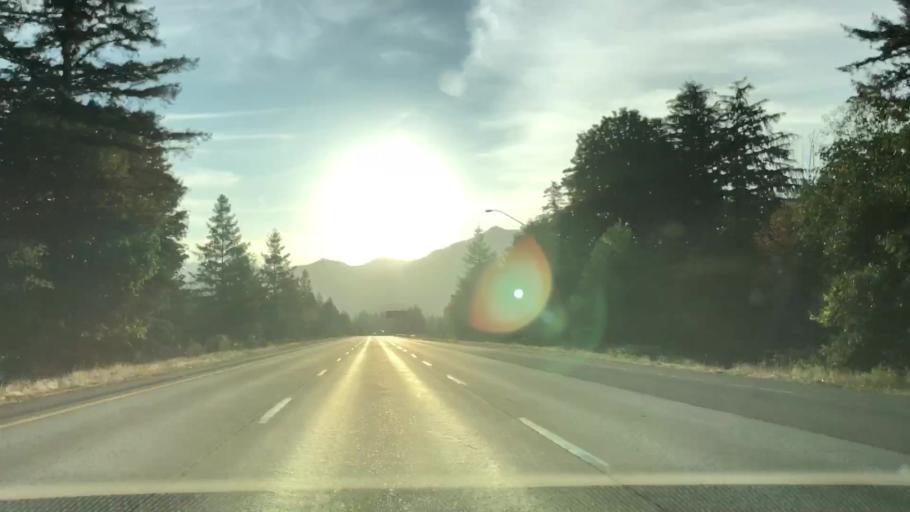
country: US
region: Washington
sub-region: King County
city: Tanner
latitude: 47.4730
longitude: -121.7504
